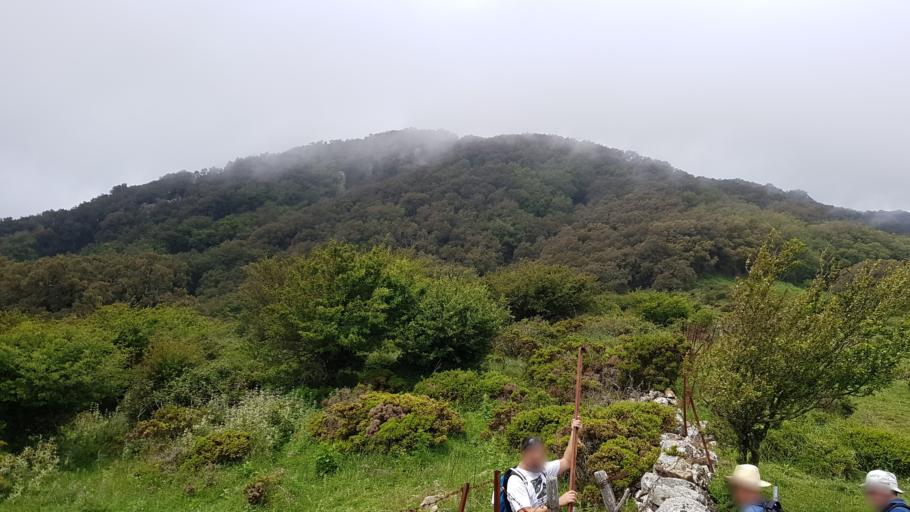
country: ES
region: Andalusia
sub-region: Provincia de Cadiz
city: Alcala de los Gazules
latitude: 36.5092
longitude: -5.5942
